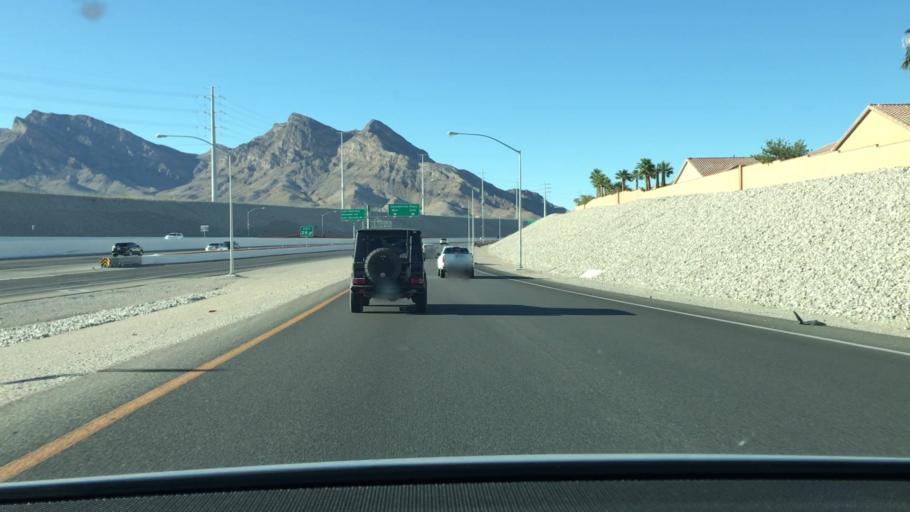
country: US
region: Nevada
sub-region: Clark County
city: Summerlin South
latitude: 36.1829
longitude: -115.3413
